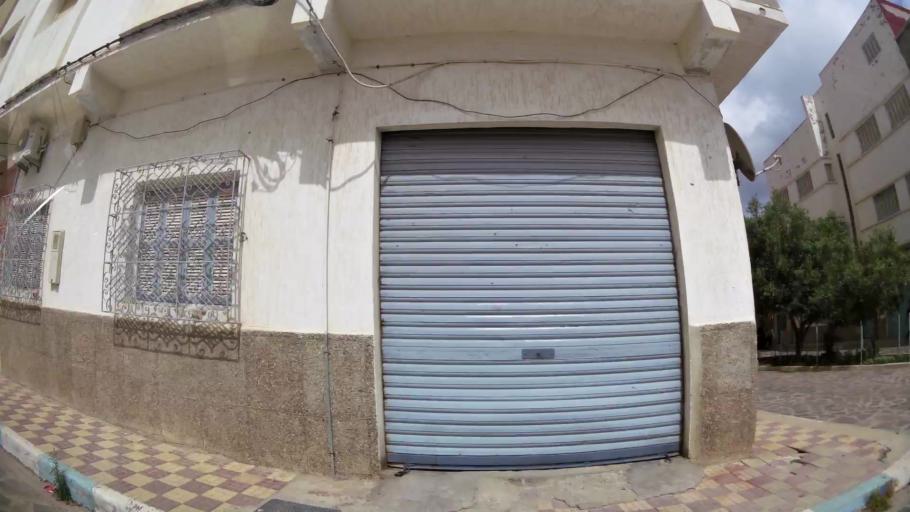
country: MA
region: Oriental
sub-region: Nador
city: Nador
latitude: 35.1722
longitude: -2.9314
